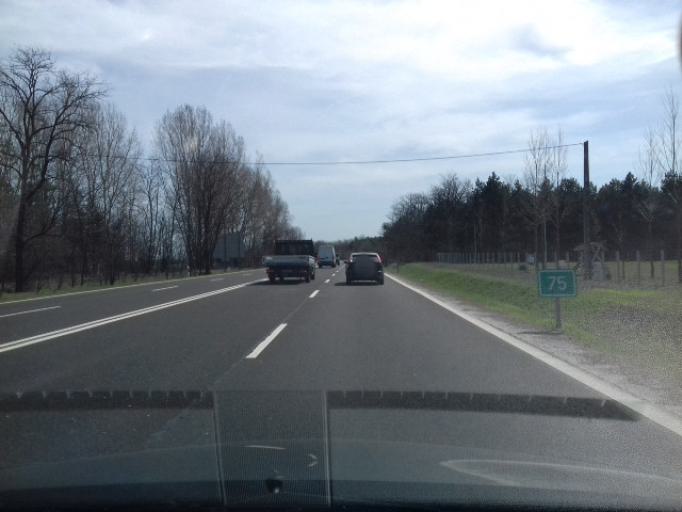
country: HU
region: Bacs-Kiskun
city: Lajosmizse
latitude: 46.9847
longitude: 19.6168
